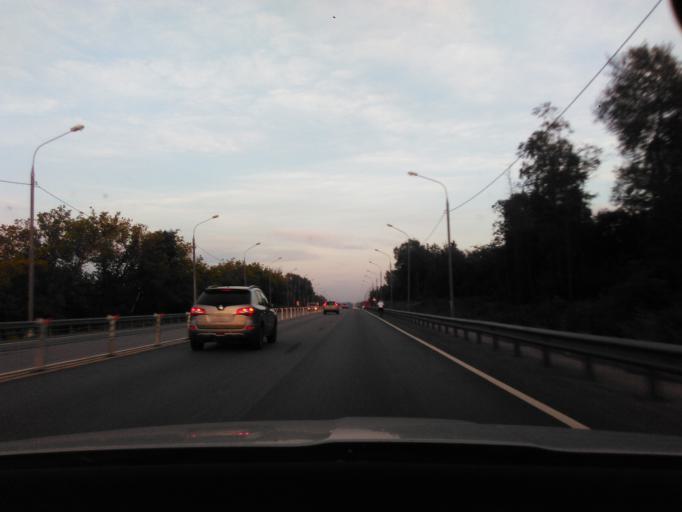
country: RU
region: Moskovskaya
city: Klin
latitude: 56.3133
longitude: 36.7739
